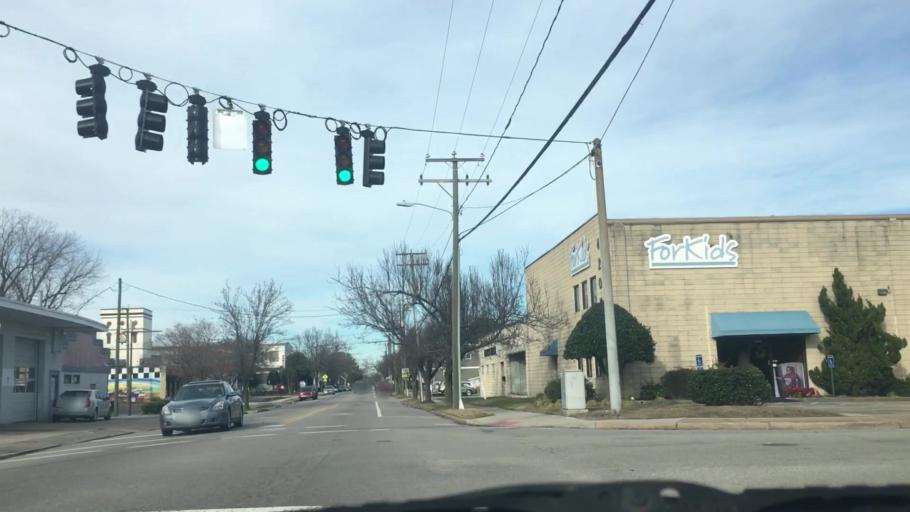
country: US
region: Virginia
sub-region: City of Norfolk
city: Norfolk
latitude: 36.8828
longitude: -76.2948
